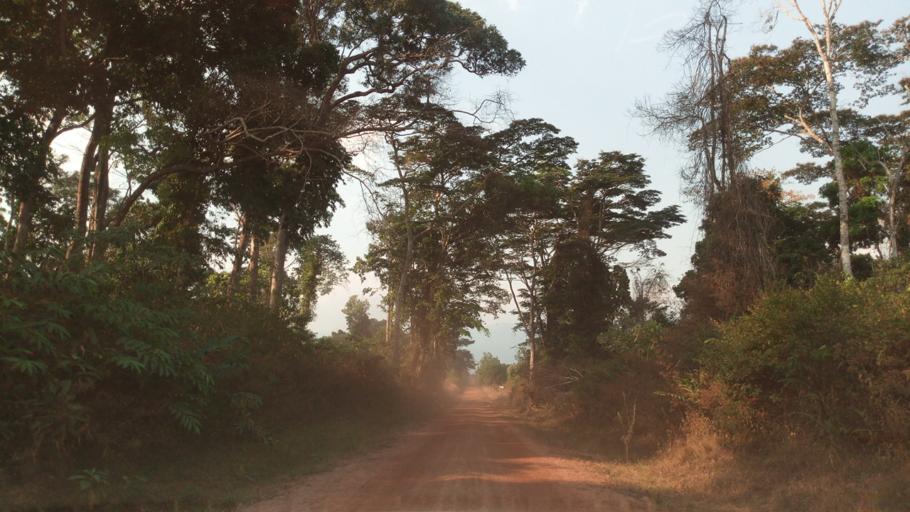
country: TZ
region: Kigoma
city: Kigoma
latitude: -5.1956
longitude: 28.8878
